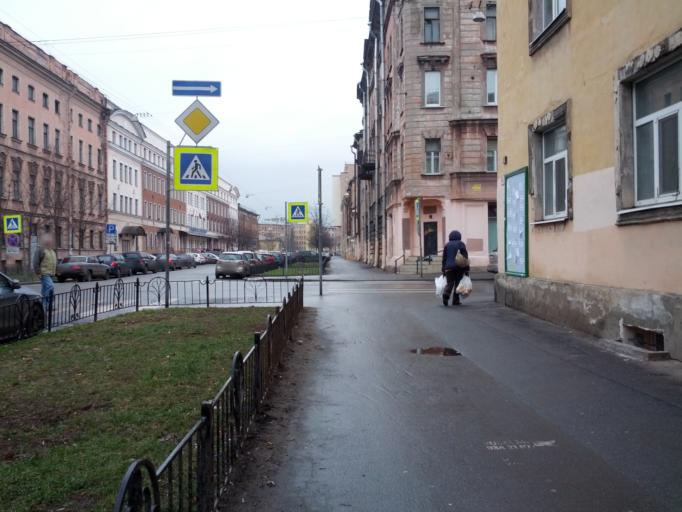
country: RU
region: St.-Petersburg
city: Centralniy
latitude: 59.9169
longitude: 30.3485
